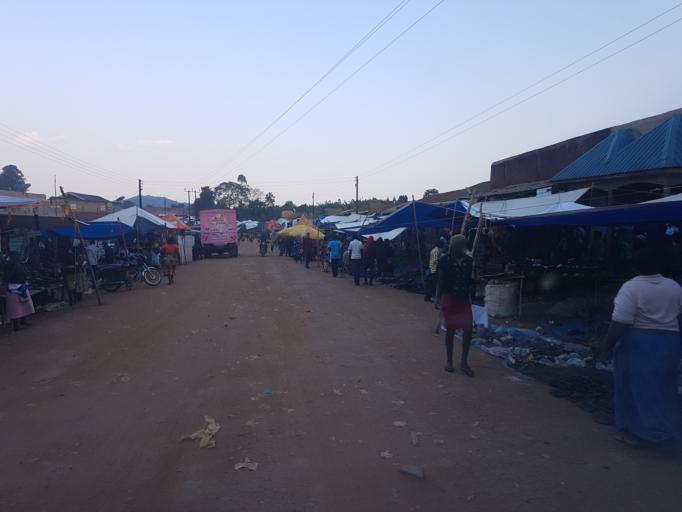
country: UG
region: Western Region
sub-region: Mitoma District
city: Mitoma
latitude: -0.6800
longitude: 29.9431
